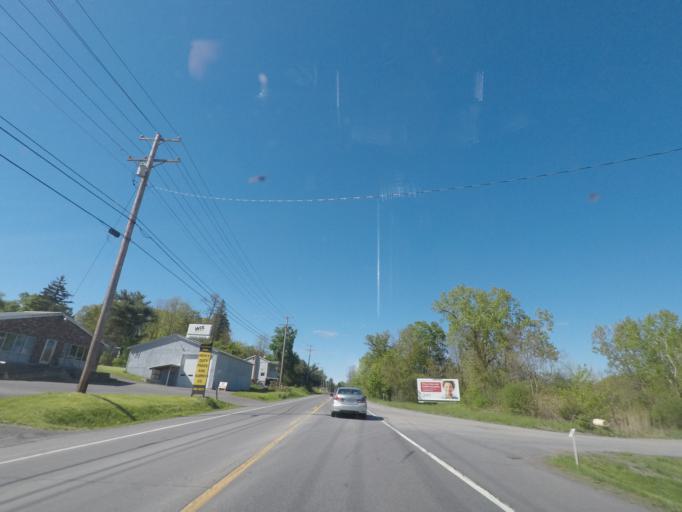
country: US
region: New York
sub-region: Albany County
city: Ravena
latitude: 42.4588
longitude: -73.8175
